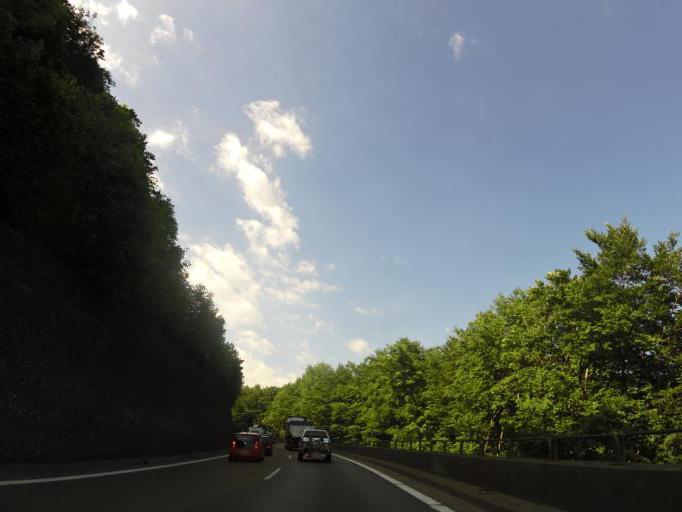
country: DE
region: Baden-Wuerttemberg
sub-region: Regierungsbezirk Stuttgart
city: Wiesensteig
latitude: 48.5639
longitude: 9.6327
